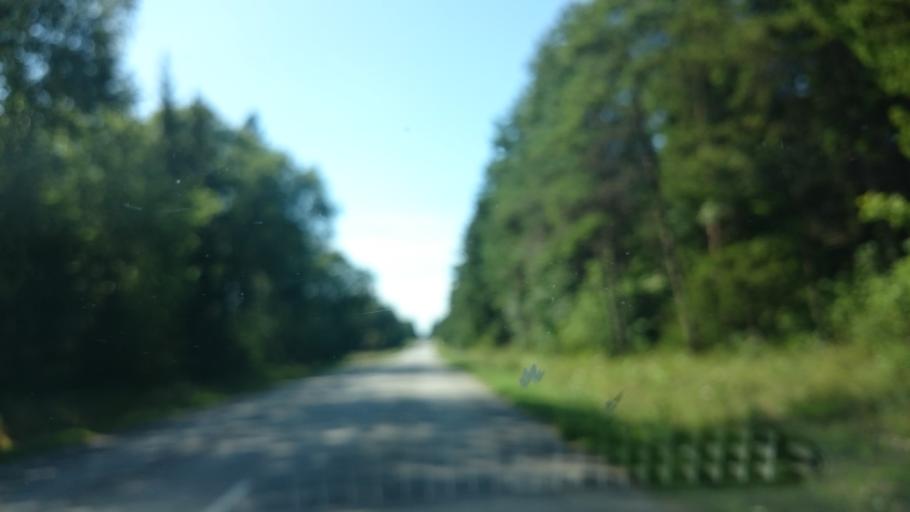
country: EE
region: Saare
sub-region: Orissaare vald
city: Orissaare
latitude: 58.5705
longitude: 22.7421
